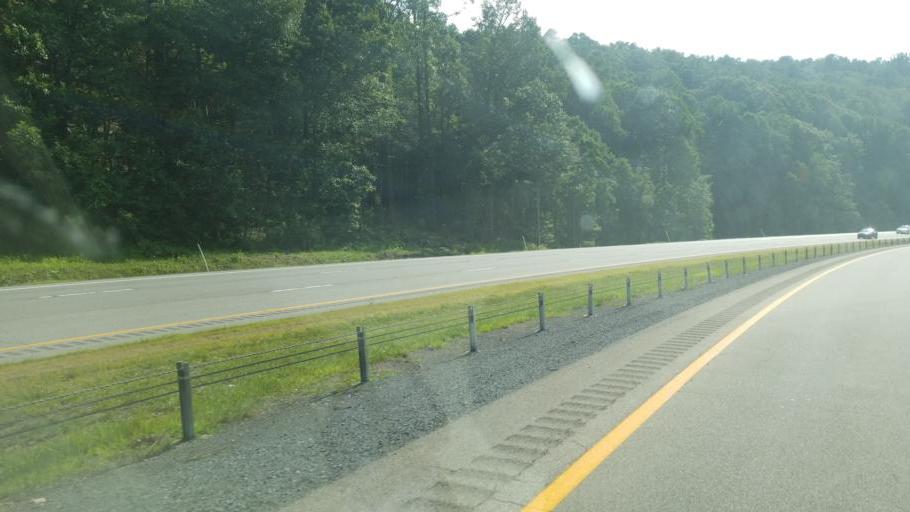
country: US
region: West Virginia
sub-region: Monongalia County
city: Cheat Lake
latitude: 39.6589
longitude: -79.8100
